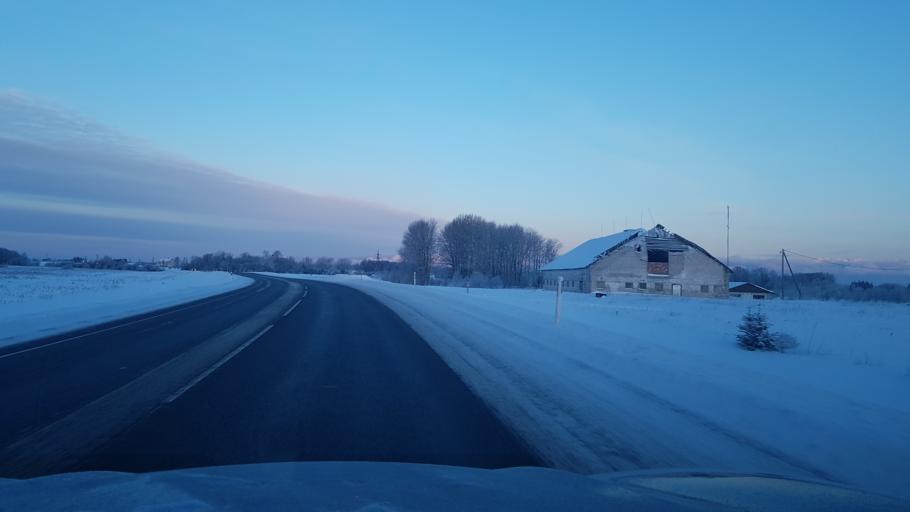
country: EE
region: Ida-Virumaa
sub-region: Narva-Joesuu linn
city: Narva-Joesuu
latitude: 59.3986
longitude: 28.0743
